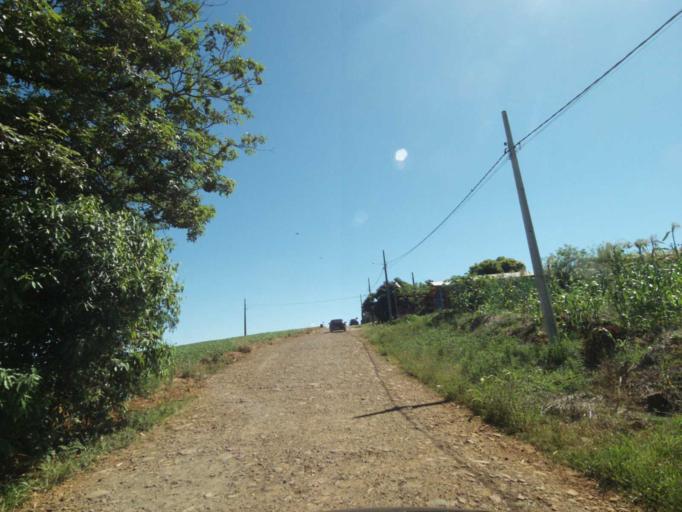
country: BR
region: Parana
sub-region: Coronel Vivida
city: Coronel Vivida
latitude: -25.9601
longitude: -52.8047
